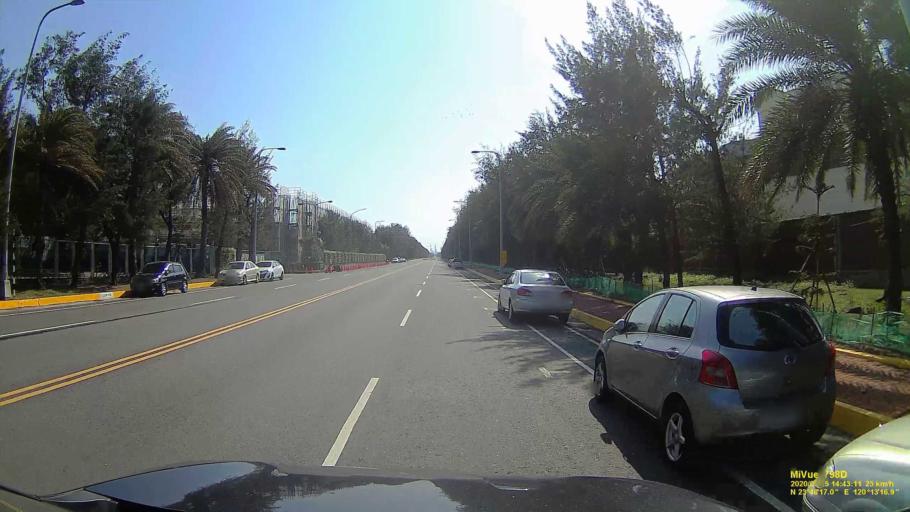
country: TW
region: Taiwan
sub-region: Yunlin
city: Douliu
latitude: 23.8046
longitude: 120.2213
